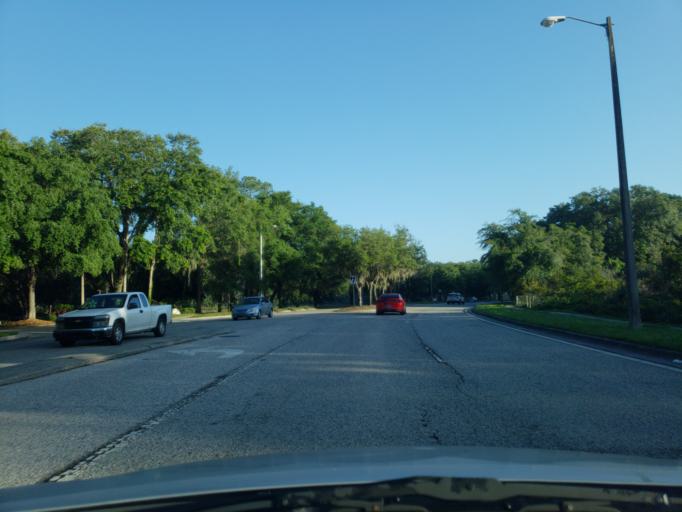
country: US
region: Florida
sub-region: Hillsborough County
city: Mango
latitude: 27.9443
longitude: -82.3259
